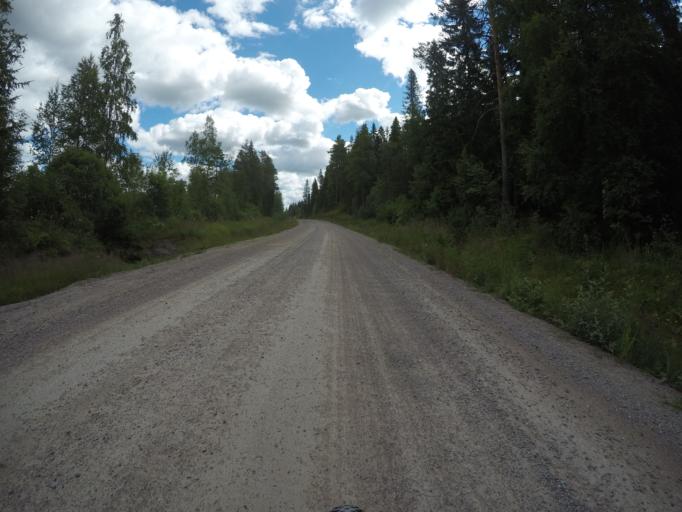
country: SE
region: Vaermland
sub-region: Filipstads Kommun
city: Lesjofors
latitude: 60.1338
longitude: 14.4077
